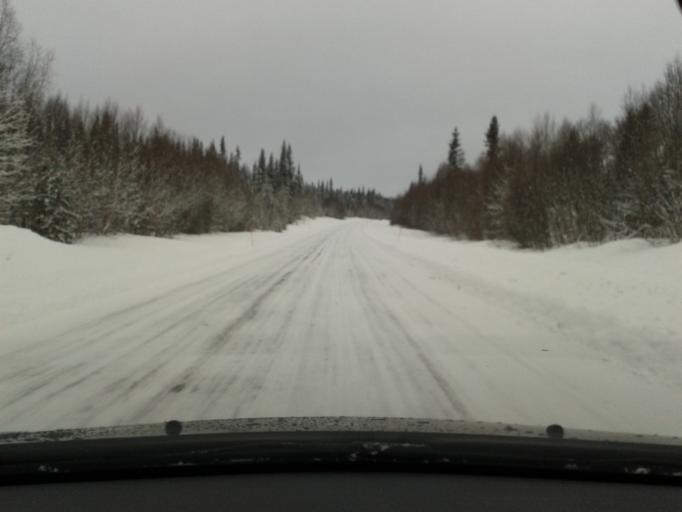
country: SE
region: Vaesterbotten
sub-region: Vilhelmina Kommun
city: Sjoberg
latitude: 65.0294
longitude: 15.8701
